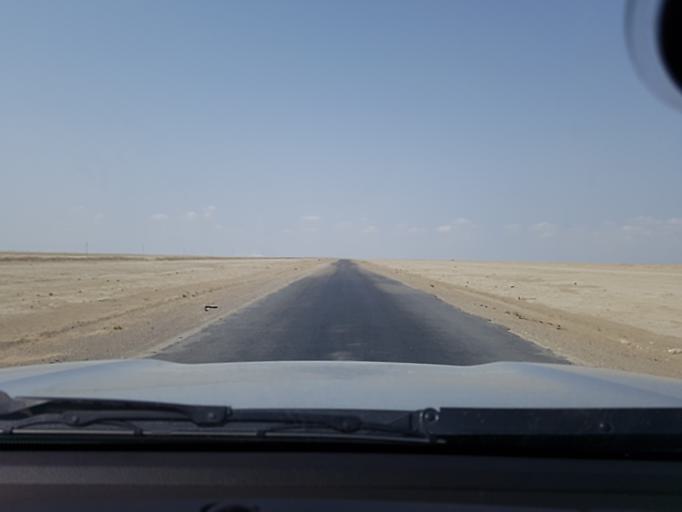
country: TM
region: Balkan
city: Gumdag
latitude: 38.6810
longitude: 54.4159
